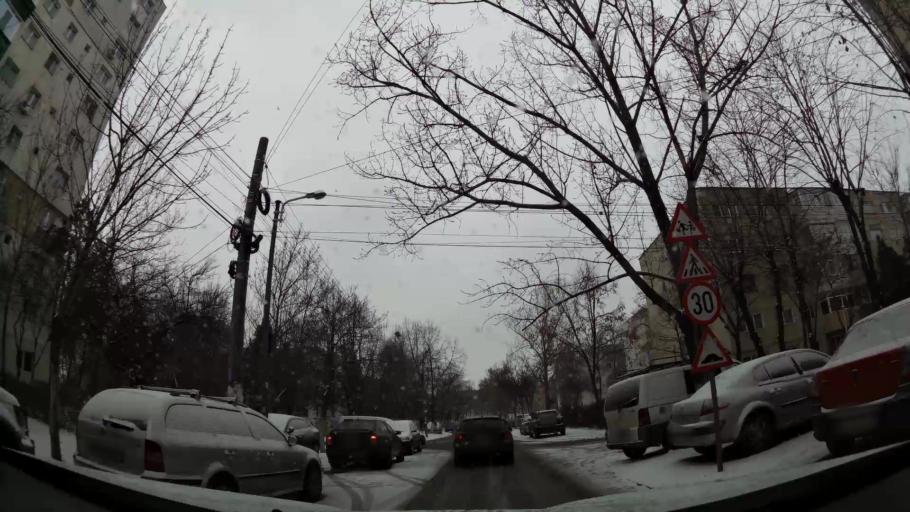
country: RO
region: Prahova
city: Ploiesti
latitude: 44.9364
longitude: 25.9855
